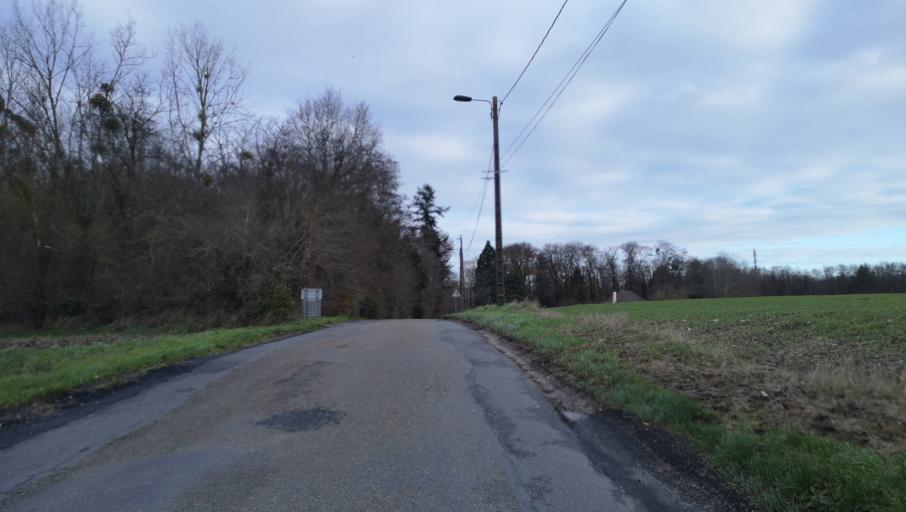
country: FR
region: Centre
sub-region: Departement du Loiret
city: Boigny-sur-Bionne
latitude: 47.9146
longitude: 2.0049
